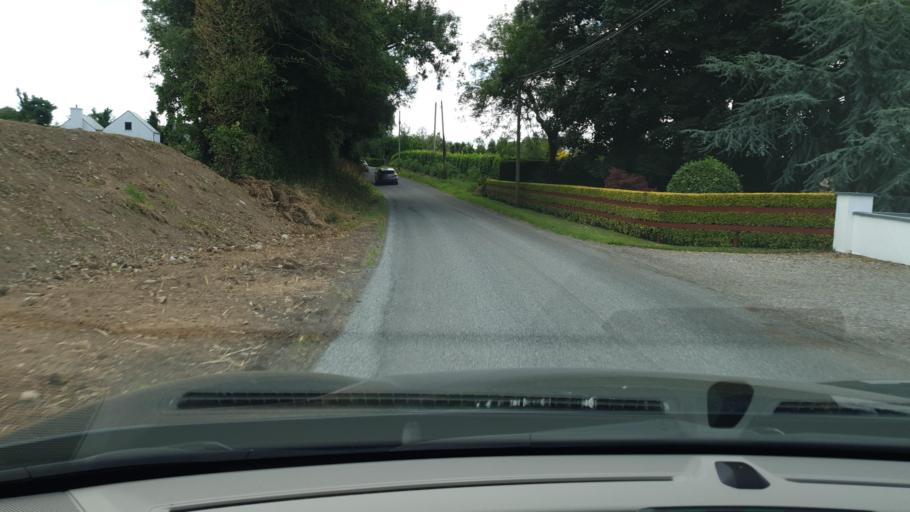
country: IE
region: Leinster
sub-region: An Mhi
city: Newtown Trim
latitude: 53.5420
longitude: -6.6989
